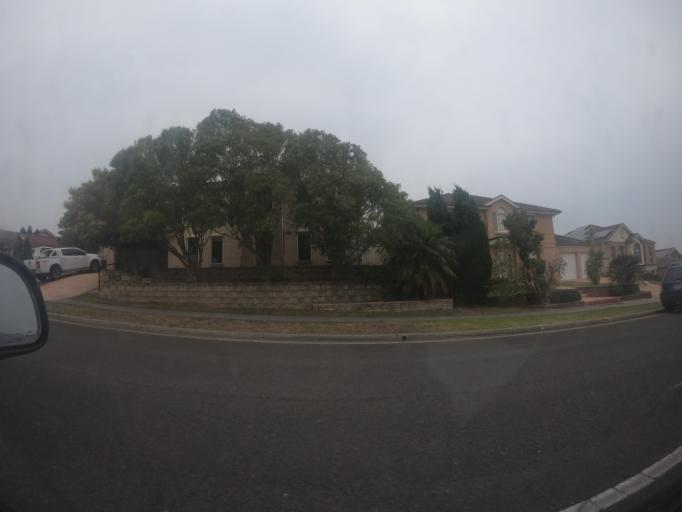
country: AU
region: New South Wales
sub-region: Shellharbour
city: Flinders
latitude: -34.5757
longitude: 150.8418
